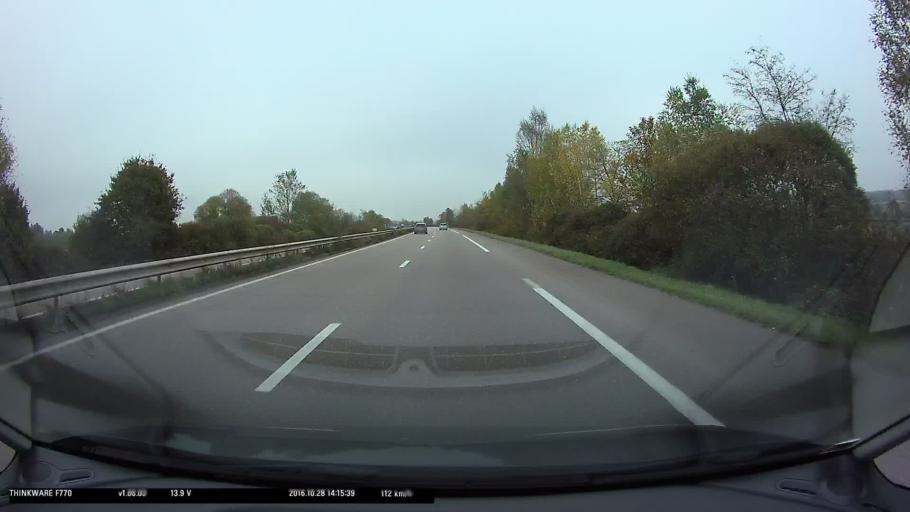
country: FR
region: Lorraine
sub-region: Departement de Meurthe-et-Moselle
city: Luneville
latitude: 48.5701
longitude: 6.5031
